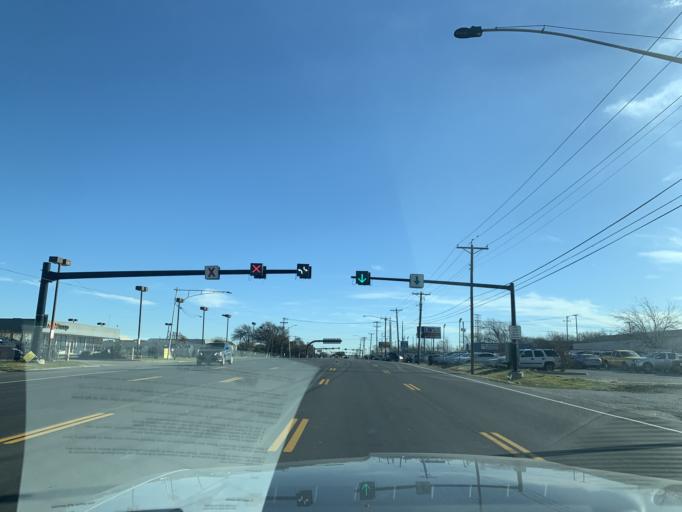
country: US
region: Texas
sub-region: Tarrant County
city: Arlington
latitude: 32.7421
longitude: -97.0805
